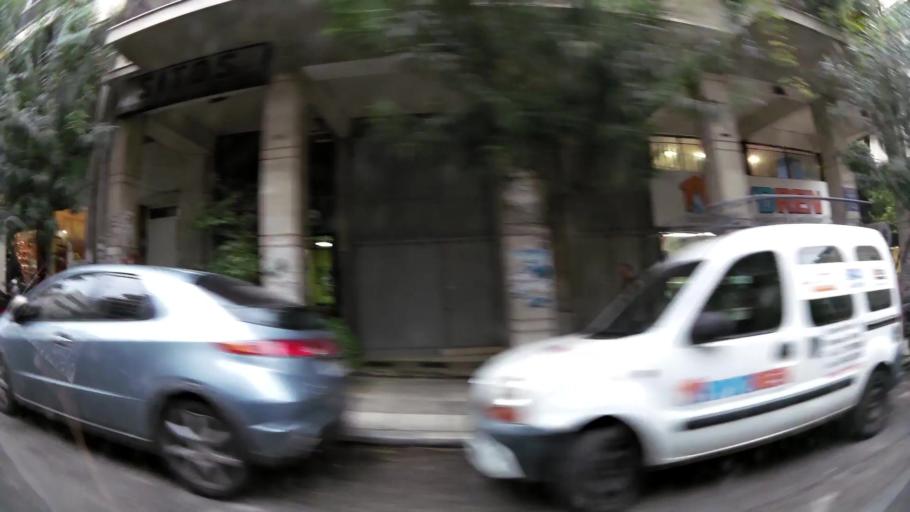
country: GR
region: Attica
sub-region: Nomarchia Athinas
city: Vyronas
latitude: 37.9691
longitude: 23.7431
